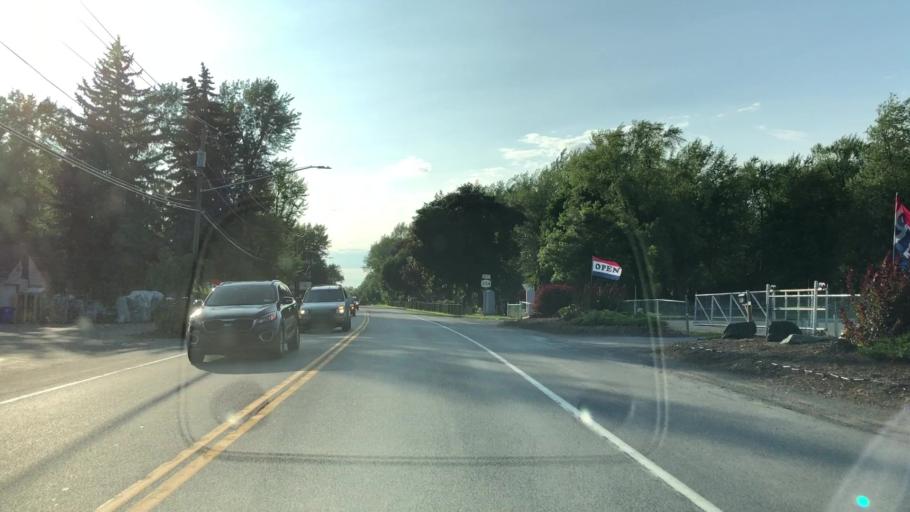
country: US
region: New York
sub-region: Erie County
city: West Seneca
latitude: 42.8683
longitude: -78.7764
